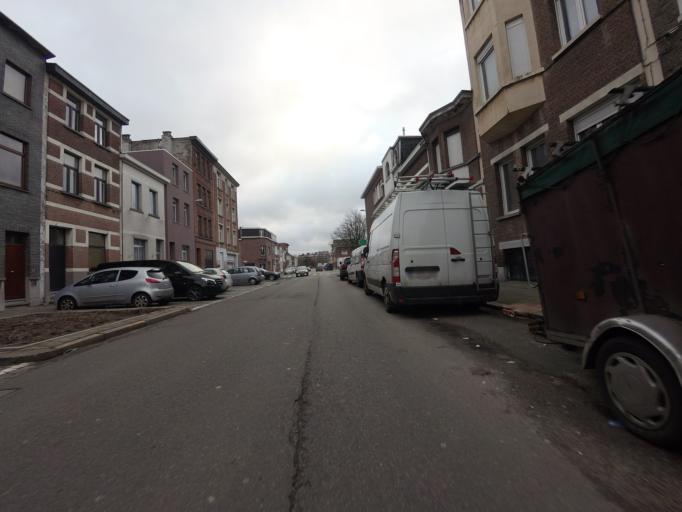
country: BE
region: Flanders
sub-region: Provincie Antwerpen
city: Hoboken
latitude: 51.1819
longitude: 4.3823
